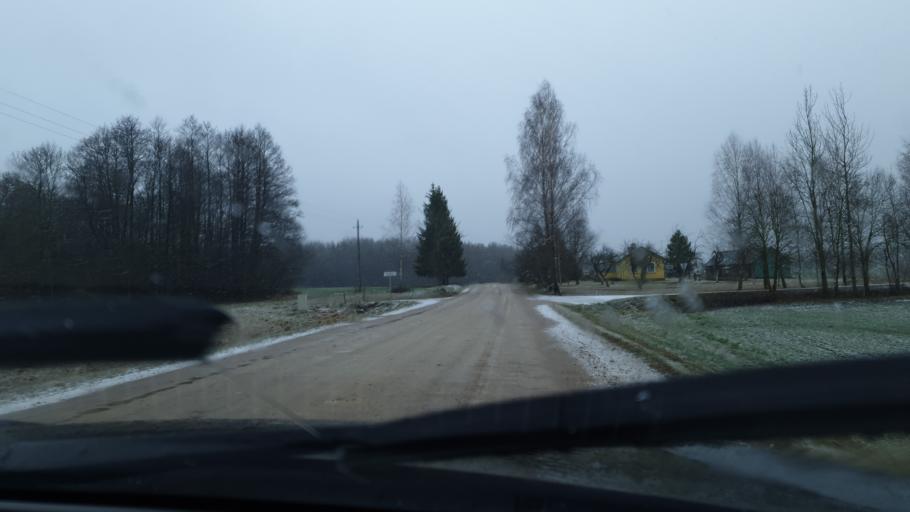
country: LT
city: Jieznas
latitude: 54.5711
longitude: 24.3178
